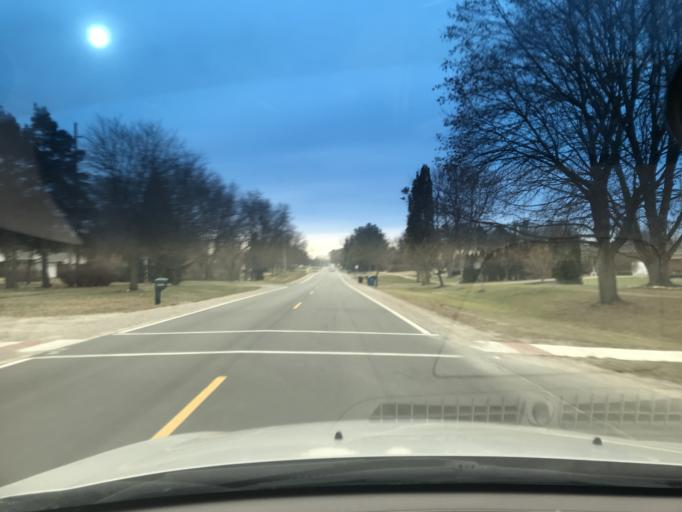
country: US
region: Michigan
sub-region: Macomb County
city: Shelby
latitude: 42.6931
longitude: -83.0544
